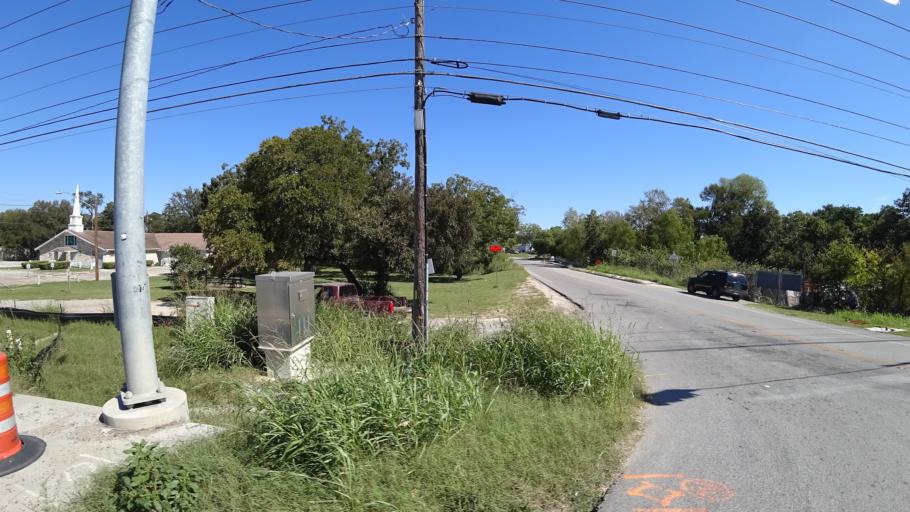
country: US
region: Texas
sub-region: Travis County
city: Hornsby Bend
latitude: 30.2669
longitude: -97.6254
